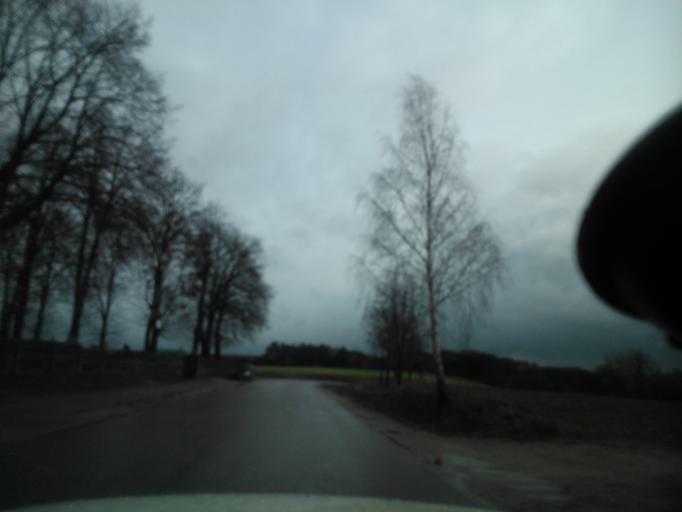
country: PL
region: Warmian-Masurian Voivodeship
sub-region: Powiat dzialdowski
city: Lidzbark
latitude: 53.3066
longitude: 19.8630
